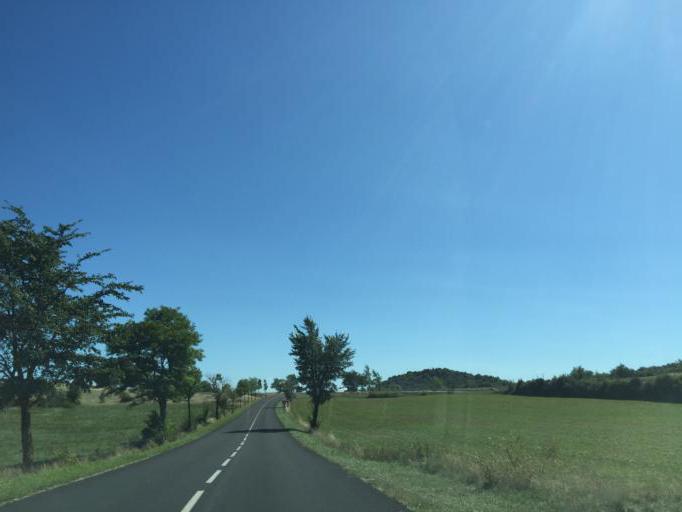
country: FR
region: Languedoc-Roussillon
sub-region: Departement de l'Herault
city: Lodeve
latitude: 43.8844
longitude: 3.3093
